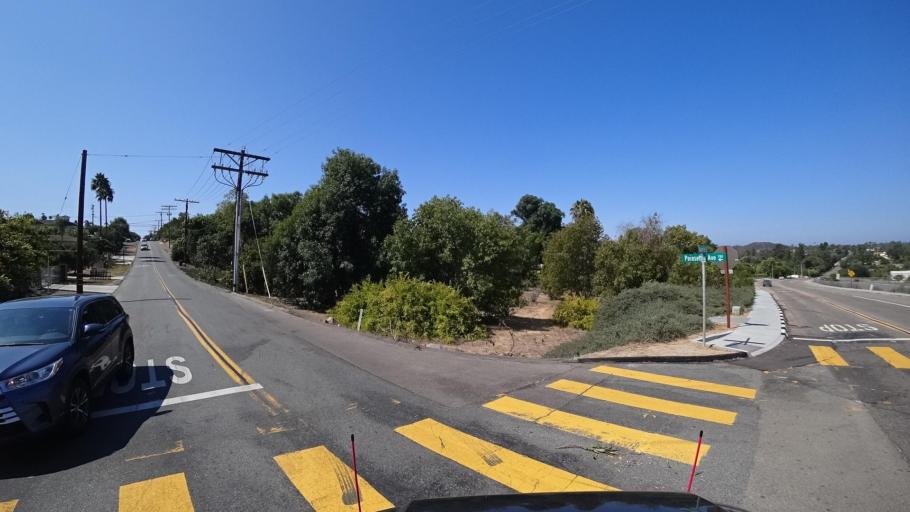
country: US
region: California
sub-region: San Diego County
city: Lake San Marcos
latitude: 33.1544
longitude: -117.2113
